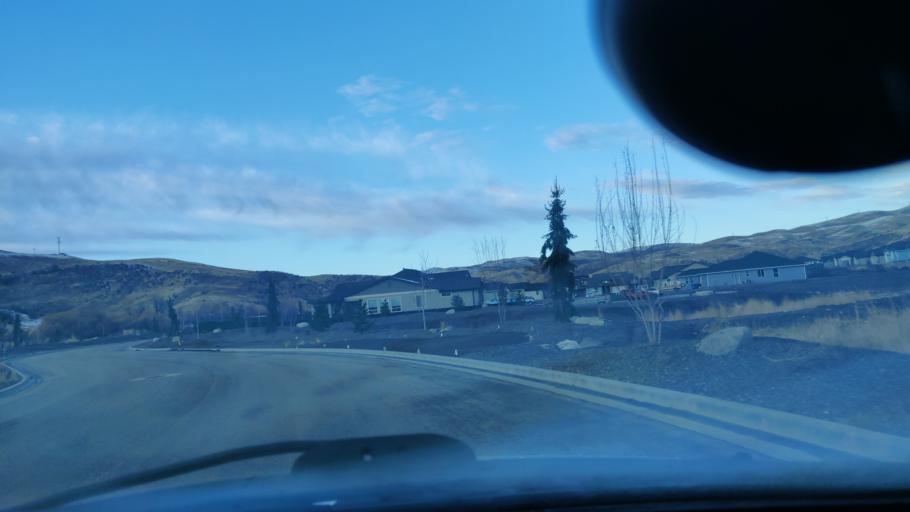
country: US
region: Idaho
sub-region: Ada County
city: Eagle
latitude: 43.7841
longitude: -116.2617
